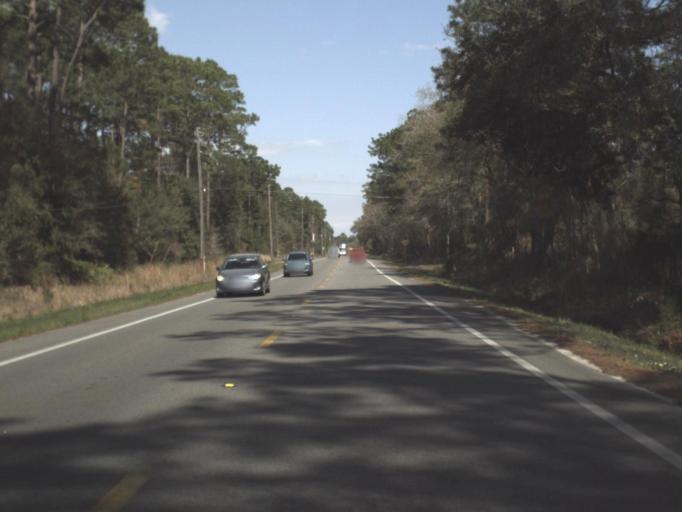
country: US
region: Florida
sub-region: Wakulla County
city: Crawfordville
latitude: 30.0797
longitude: -84.3973
